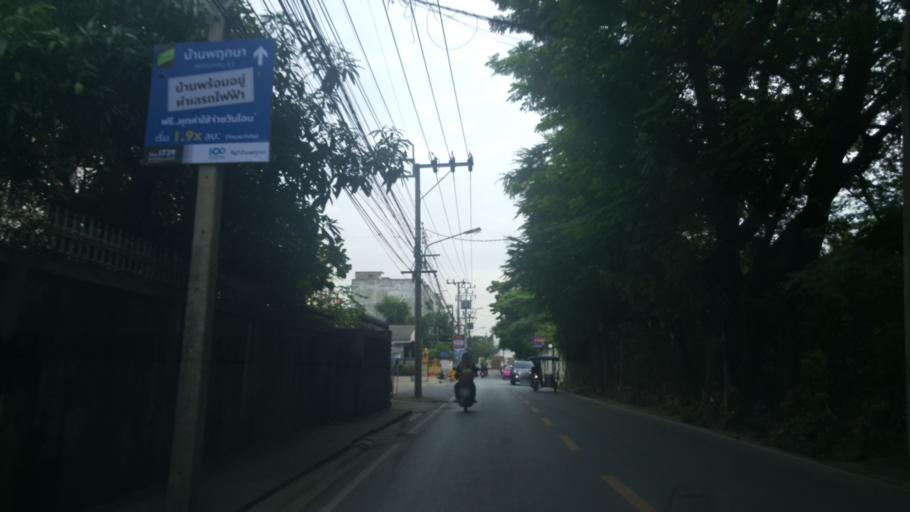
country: TH
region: Bangkok
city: Bang Khae
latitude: 13.6949
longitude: 100.3857
